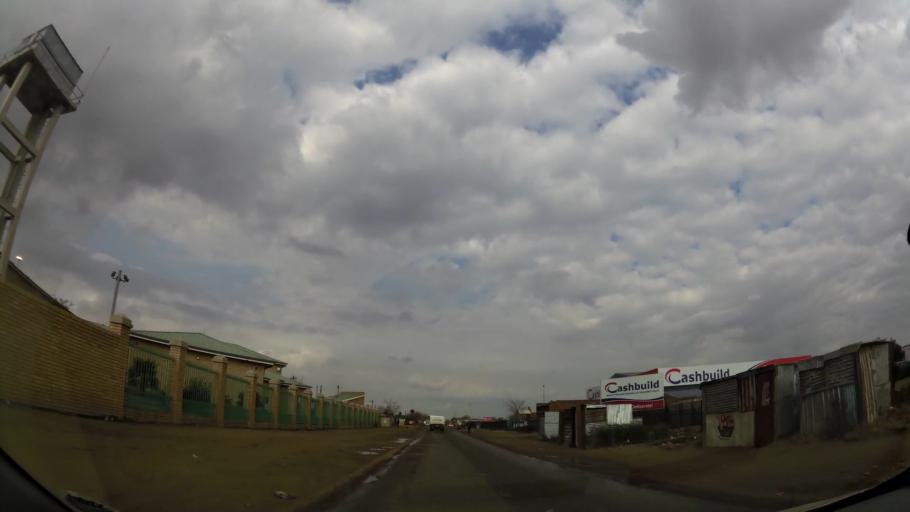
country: ZA
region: Orange Free State
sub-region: Fezile Dabi District Municipality
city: Sasolburg
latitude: -26.8445
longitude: 27.8564
